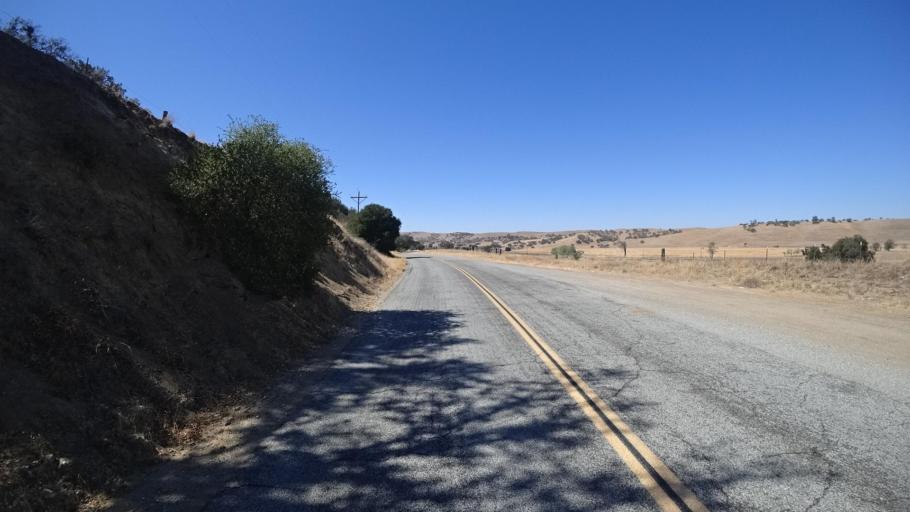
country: US
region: California
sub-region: San Luis Obispo County
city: San Miguel
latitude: 35.8232
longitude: -120.6530
